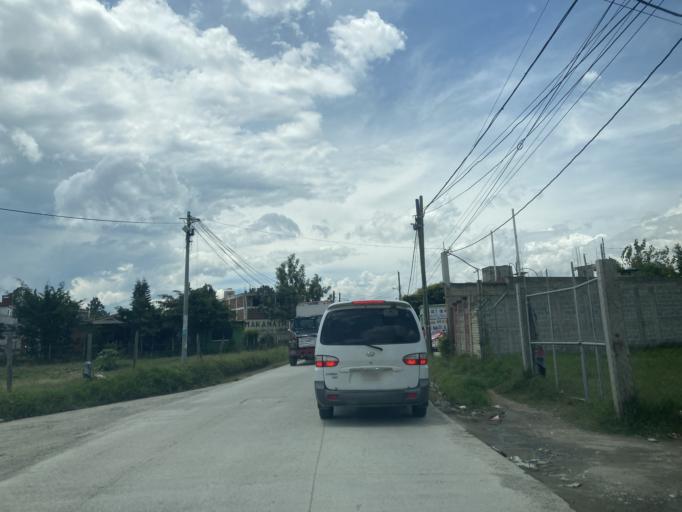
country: GT
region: Huehuetenango
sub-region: Municipio de Huehuetenango
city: Huehuetenango
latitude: 15.3274
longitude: -91.4916
